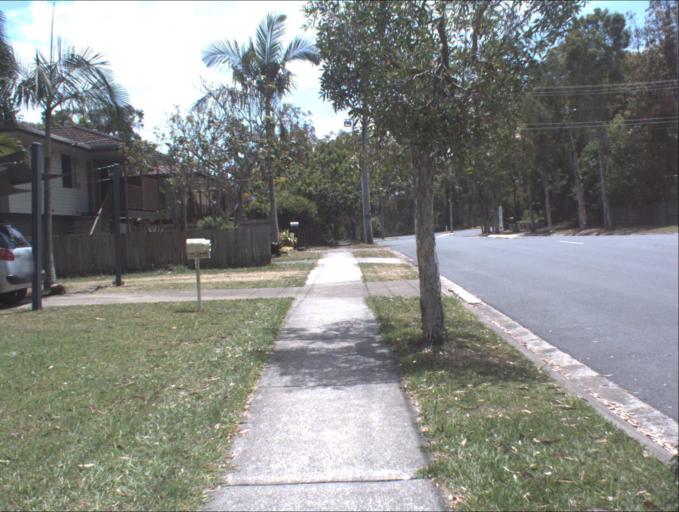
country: AU
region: Queensland
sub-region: Logan
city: Rochedale South
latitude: -27.5902
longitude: 153.1354
